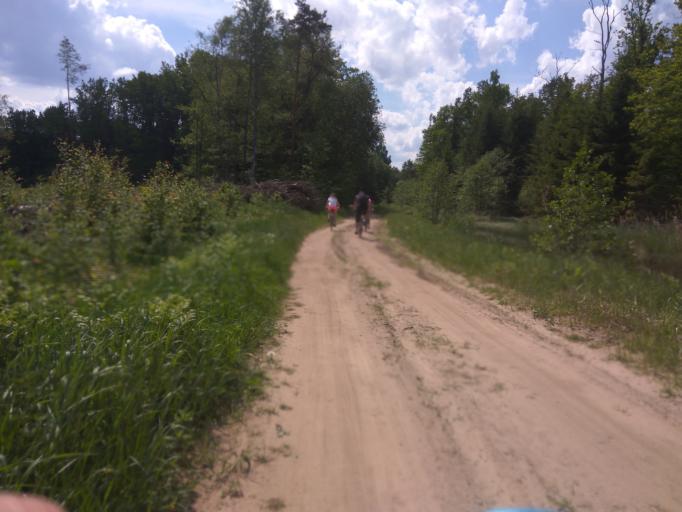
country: LV
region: Kuldigas Rajons
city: Kuldiga
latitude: 56.8824
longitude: 21.9724
